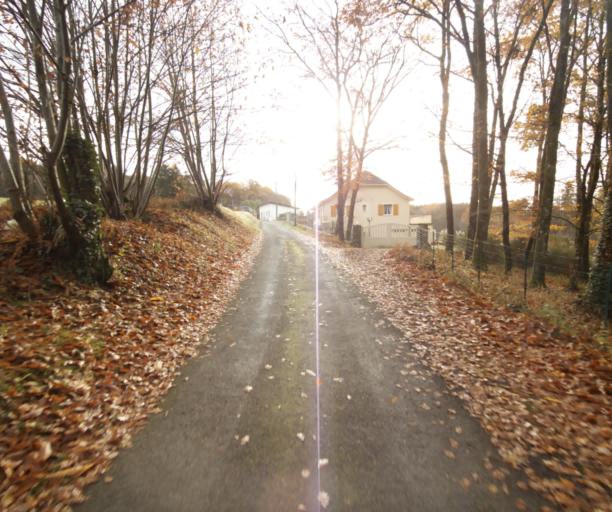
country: FR
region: Limousin
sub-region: Departement de la Correze
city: Cornil
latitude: 45.2003
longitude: 1.7117
